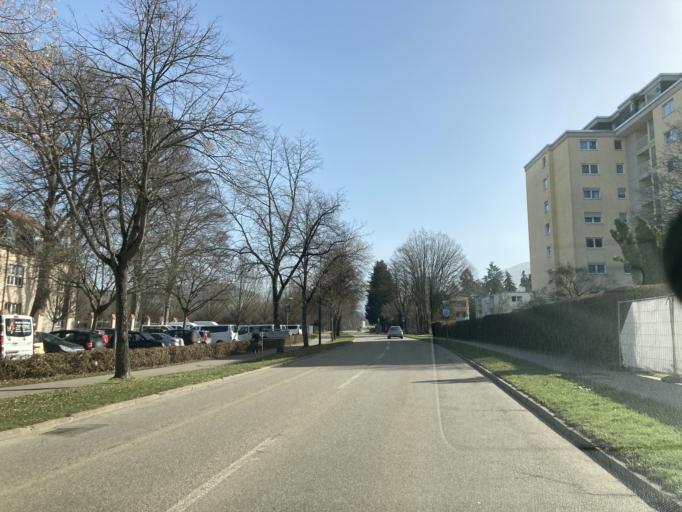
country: DE
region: Baden-Wuerttemberg
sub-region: Freiburg Region
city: Mullheim
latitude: 47.8108
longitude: 7.6316
